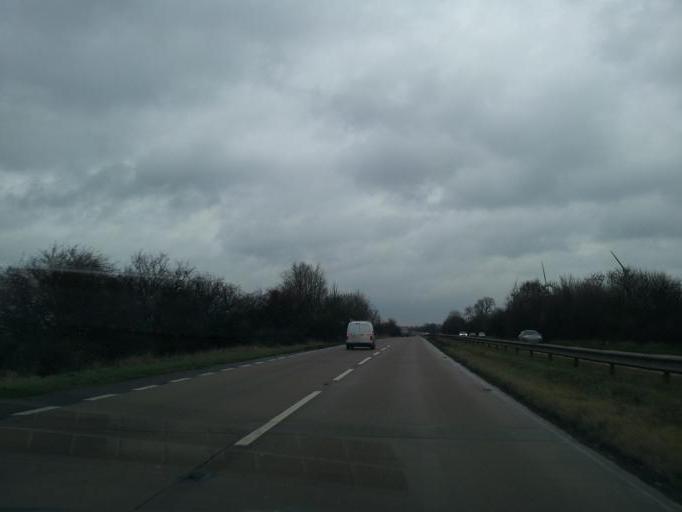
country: GB
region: England
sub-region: Leicestershire
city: Grimston
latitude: 52.8029
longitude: -1.0416
